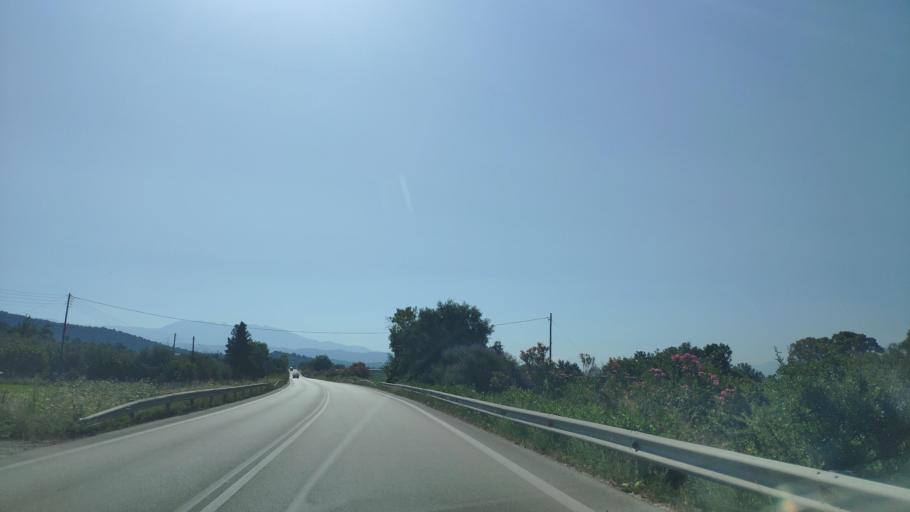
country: GR
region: West Greece
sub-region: Nomos Aitolias kai Akarnanias
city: Fitiai
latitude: 38.6874
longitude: 21.2349
